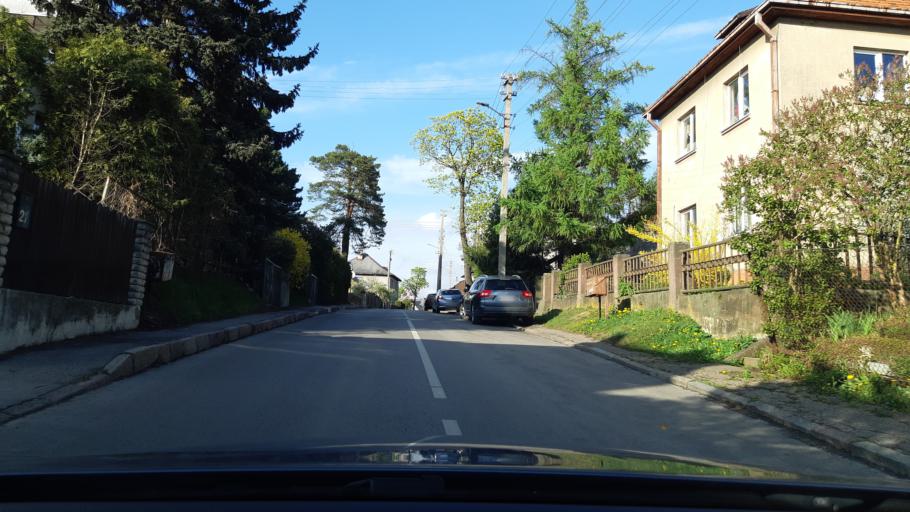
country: LT
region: Kauno apskritis
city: Dainava (Kaunas)
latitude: 54.8762
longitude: 23.9457
